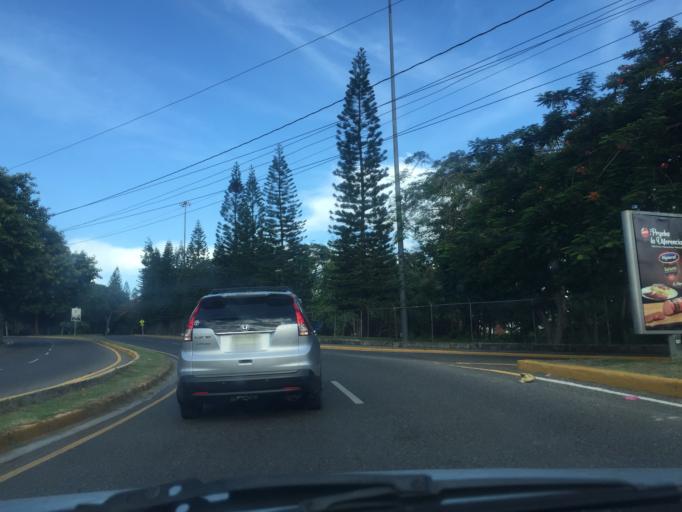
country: DO
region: Santiago
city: Santiago de los Caballeros
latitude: 19.4490
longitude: -70.6850
